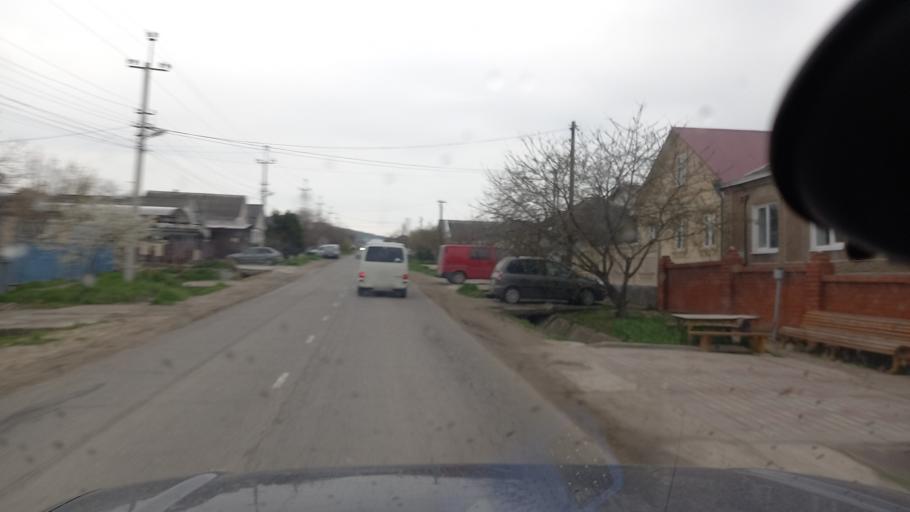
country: RU
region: Krasnodarskiy
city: Sukko
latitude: 44.8590
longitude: 37.4374
